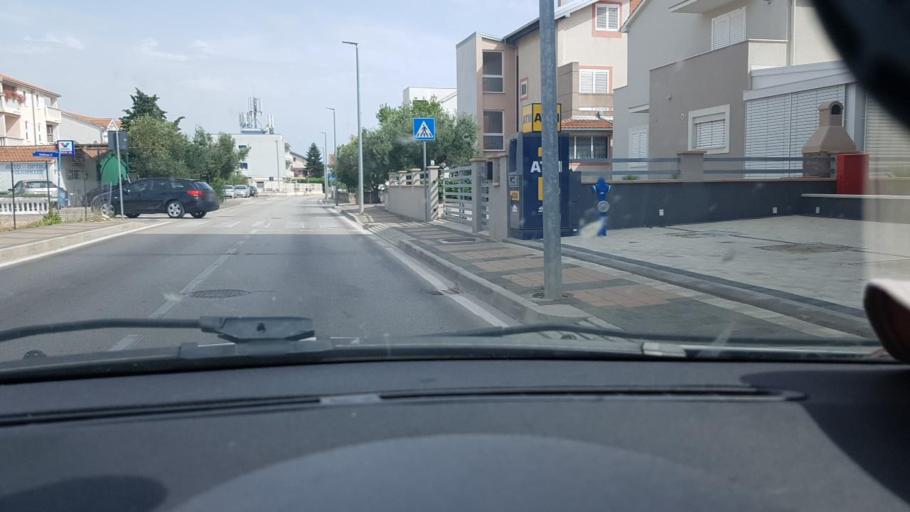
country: HR
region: Sibensko-Kniniska
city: Vodice
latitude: 43.7596
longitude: 15.7877
